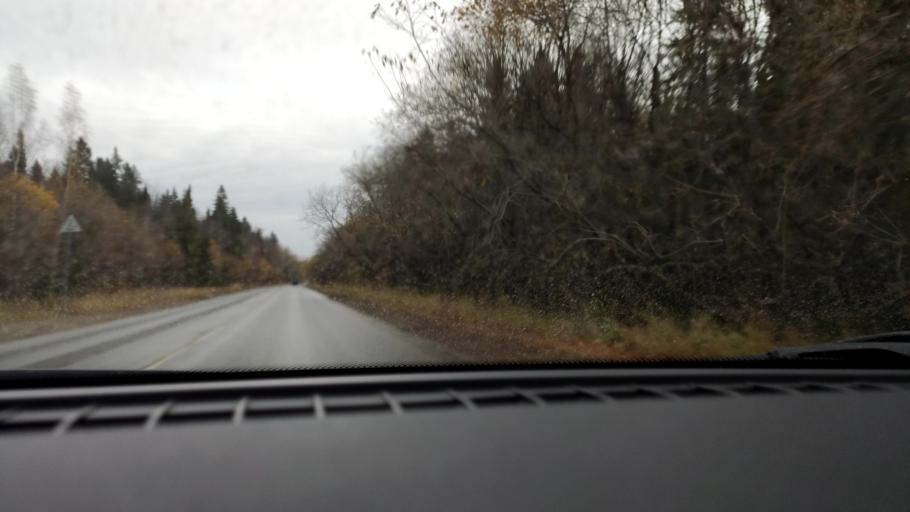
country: RU
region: Perm
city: Ferma
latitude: 57.9609
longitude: 56.3453
